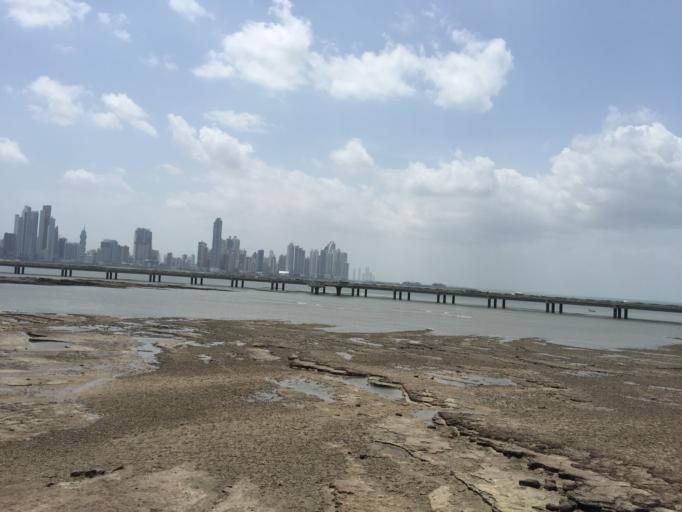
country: PA
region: Panama
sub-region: Distrito de Panama
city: Ancon
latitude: 8.9504
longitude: -79.5316
